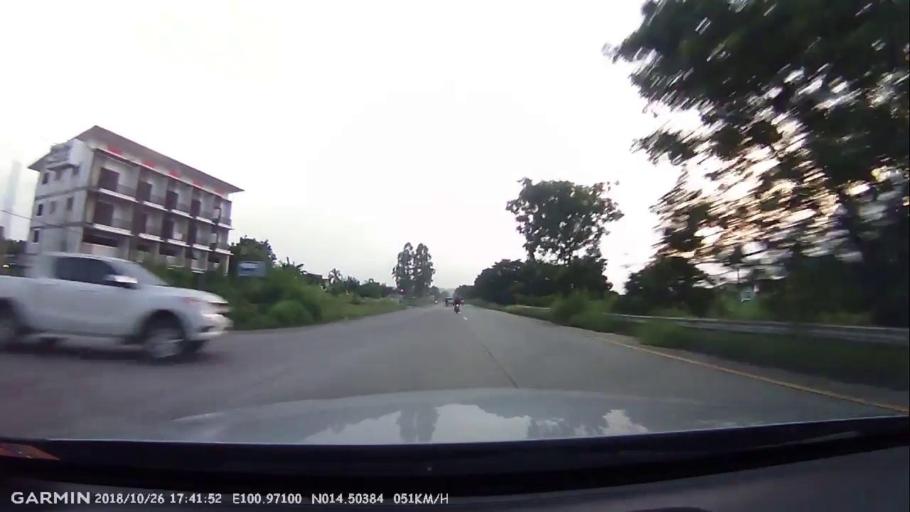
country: TH
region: Sara Buri
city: Saraburi
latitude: 14.5035
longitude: 100.9709
